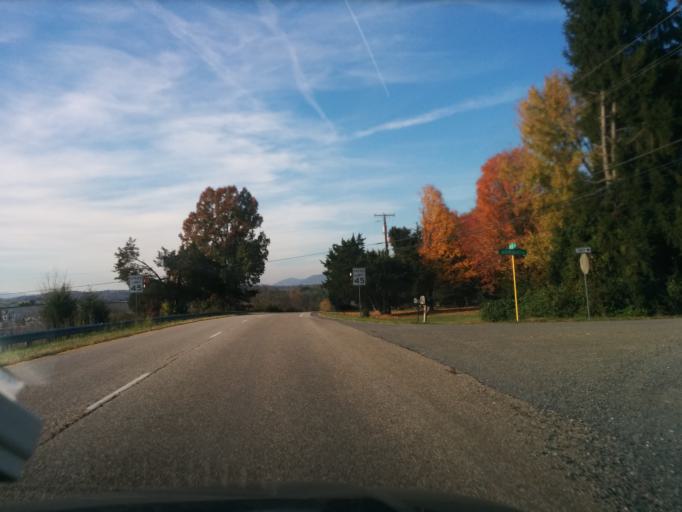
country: US
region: Virginia
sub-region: Rockbridge County
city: East Lexington
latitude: 37.8070
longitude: -79.4024
